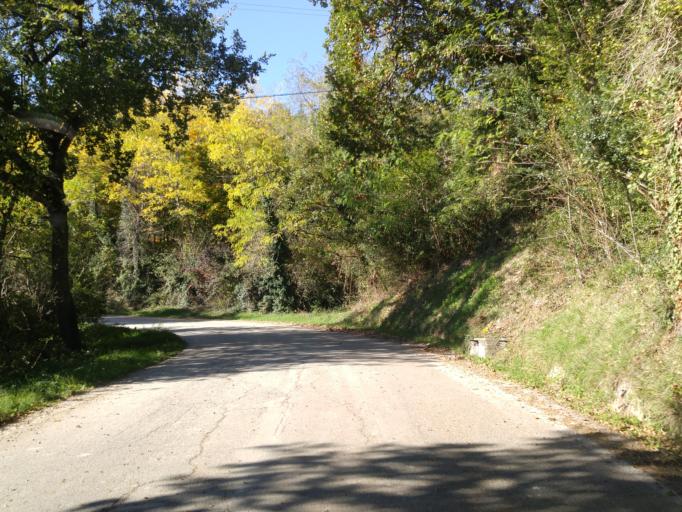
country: IT
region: The Marches
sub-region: Provincia di Pesaro e Urbino
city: Serrungarina
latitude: 43.7537
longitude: 12.8628
